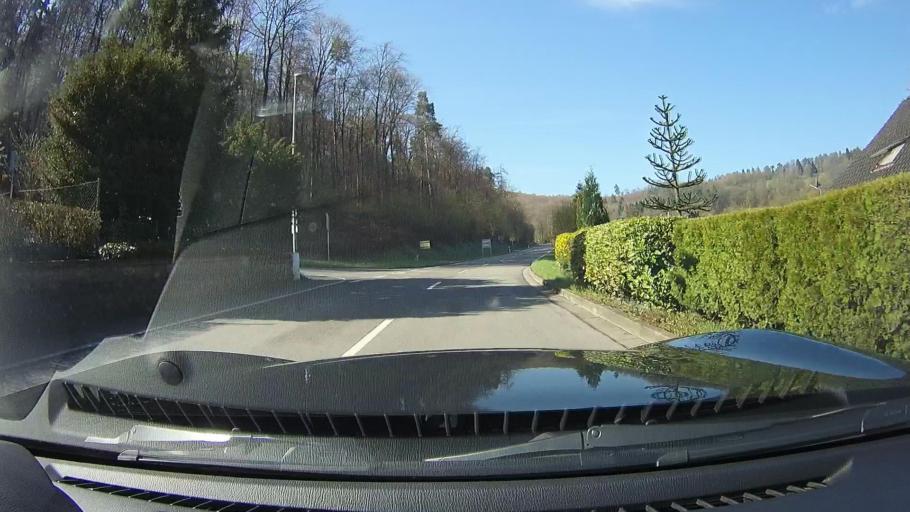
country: DE
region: Baden-Wuerttemberg
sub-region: Karlsruhe Region
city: Eberbach
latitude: 49.4497
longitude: 8.9782
